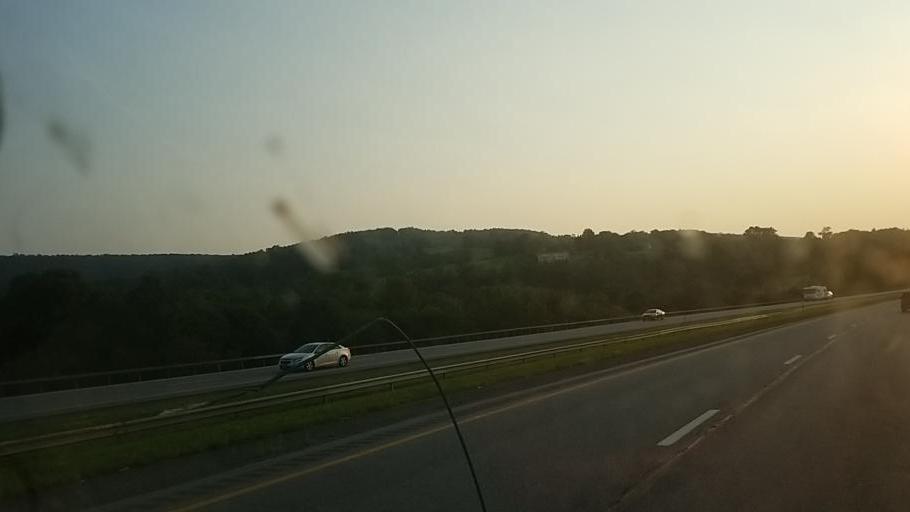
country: US
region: New York
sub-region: Herkimer County
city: Little Falls
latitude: 43.0047
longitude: -74.8846
